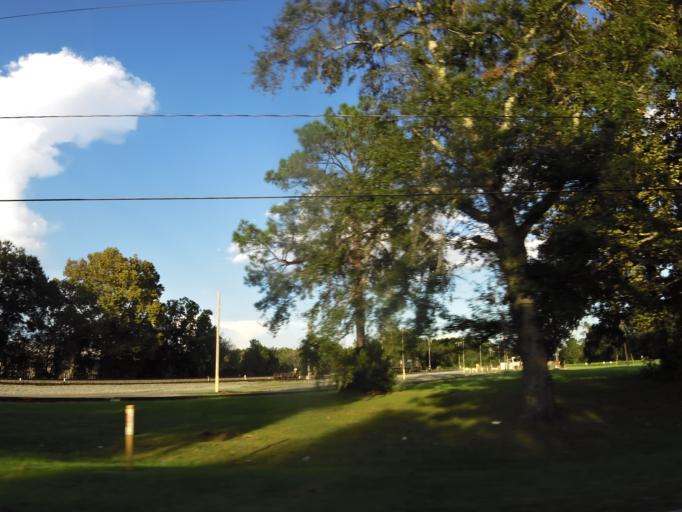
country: US
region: Georgia
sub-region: Lowndes County
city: Valdosta
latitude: 30.8302
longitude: -83.2688
